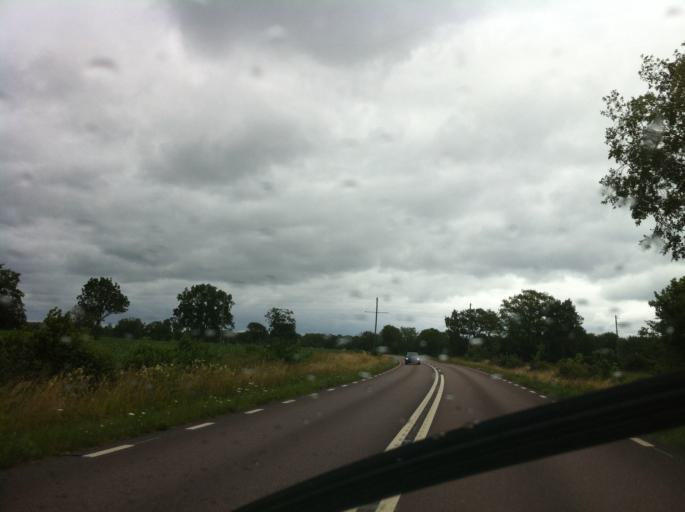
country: SE
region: Kalmar
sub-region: Borgholms Kommun
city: Borgholm
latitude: 57.1440
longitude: 17.0047
